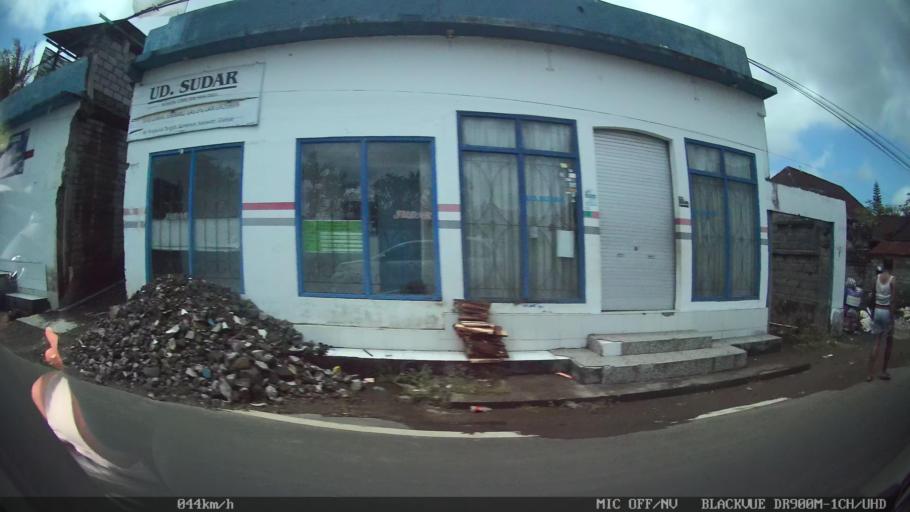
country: ID
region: Bali
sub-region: Kabupaten Gianyar
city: Ubud
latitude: -8.5389
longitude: 115.2820
